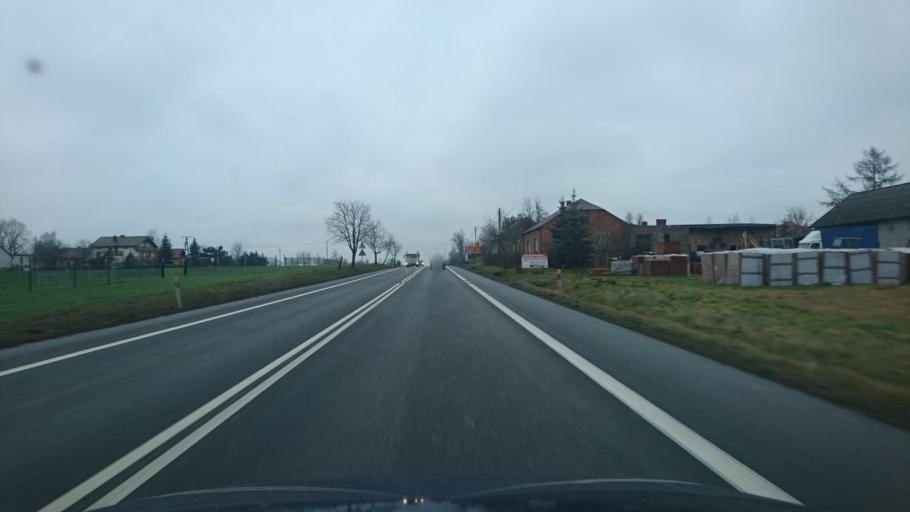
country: PL
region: Lodz Voivodeship
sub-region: Powiat wieruszowski
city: Walichnowy
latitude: 51.3026
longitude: 18.3801
